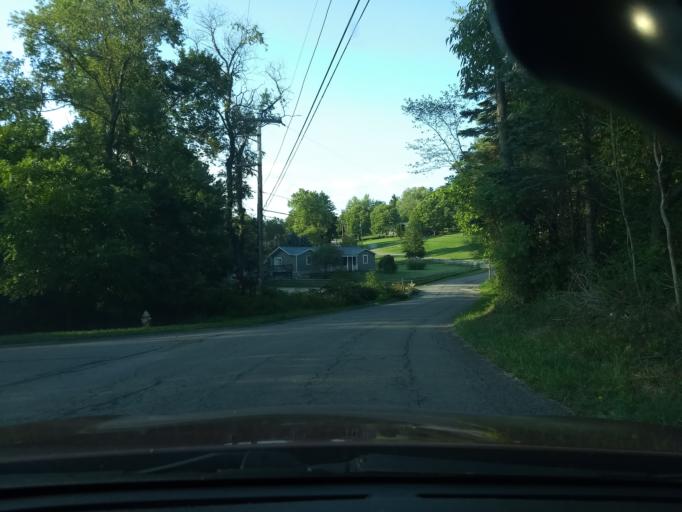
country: US
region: Pennsylvania
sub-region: Allegheny County
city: Gibsonia
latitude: 40.6394
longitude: -79.9609
